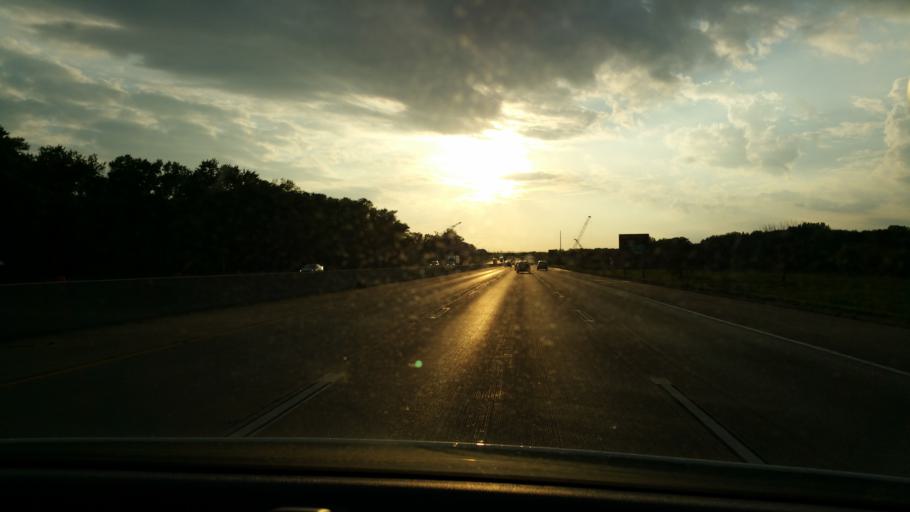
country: US
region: Iowa
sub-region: Polk County
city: Johnston
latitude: 41.6513
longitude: -93.6750
